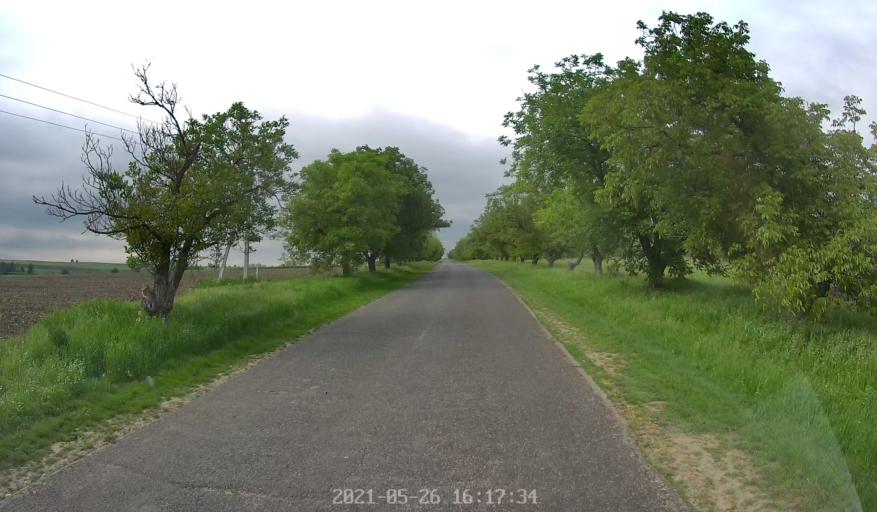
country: MD
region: Hincesti
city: Dancu
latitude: 46.7334
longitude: 28.3604
